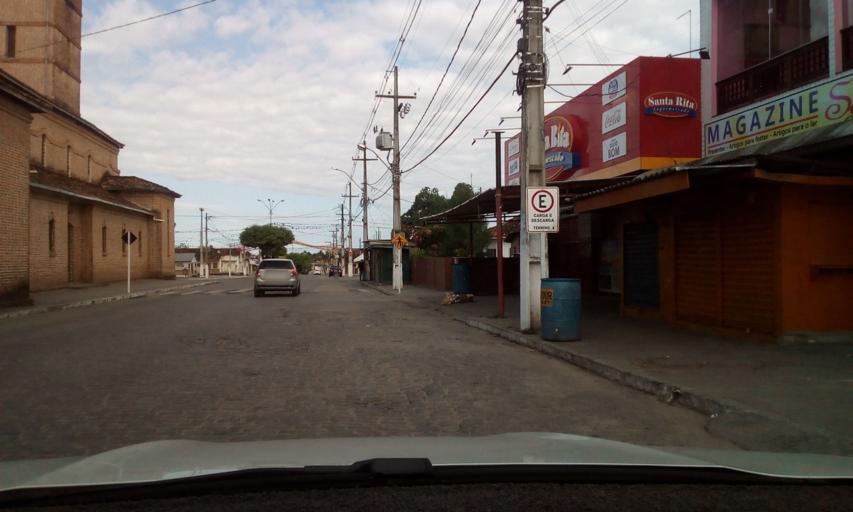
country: BR
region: Paraiba
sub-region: Rio Tinto
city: Rio Tinto
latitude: -6.8071
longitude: -35.0777
